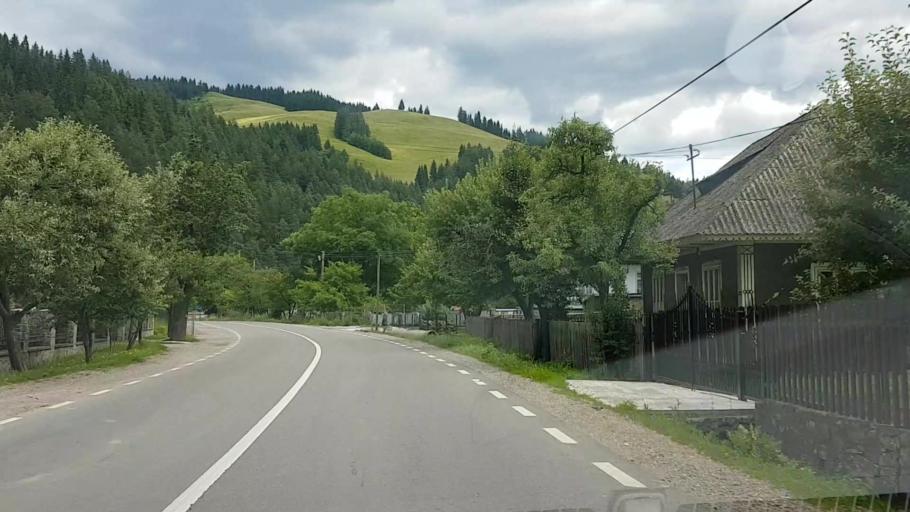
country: RO
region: Neamt
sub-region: Comuna Farcasa
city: Farcasa
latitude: 47.1352
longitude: 25.8933
